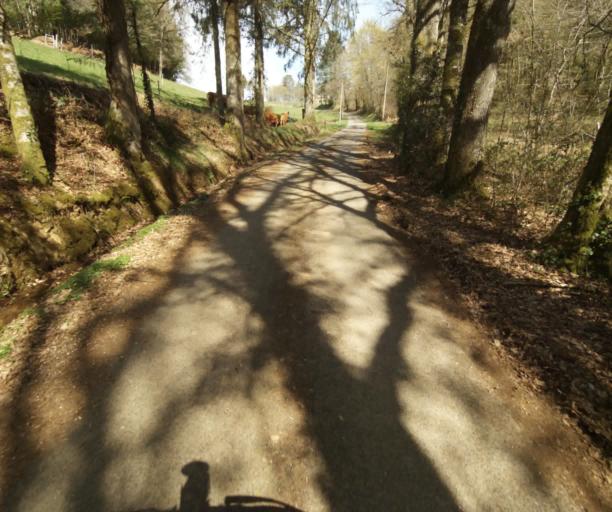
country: FR
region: Limousin
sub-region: Departement de la Correze
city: Seilhac
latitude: 45.4023
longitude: 1.7717
